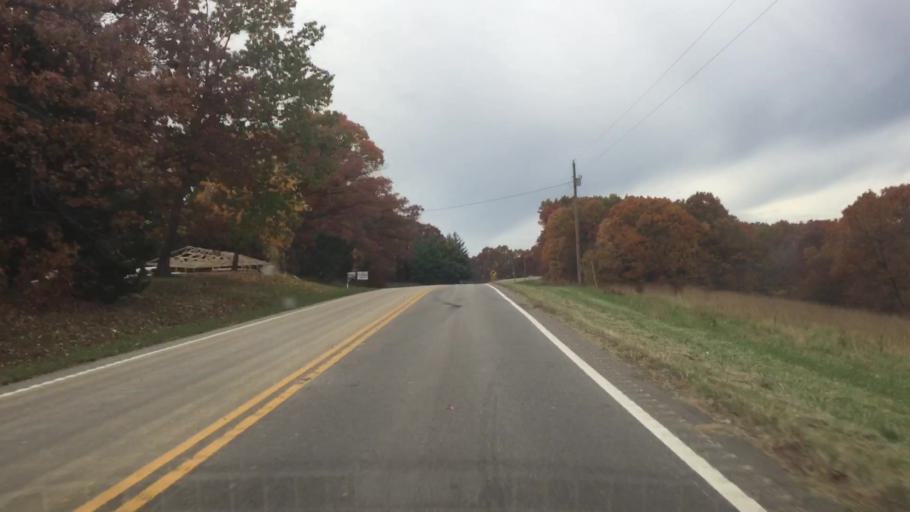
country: US
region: Missouri
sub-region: Gasconade County
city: Hermann
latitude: 38.7144
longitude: -91.6385
